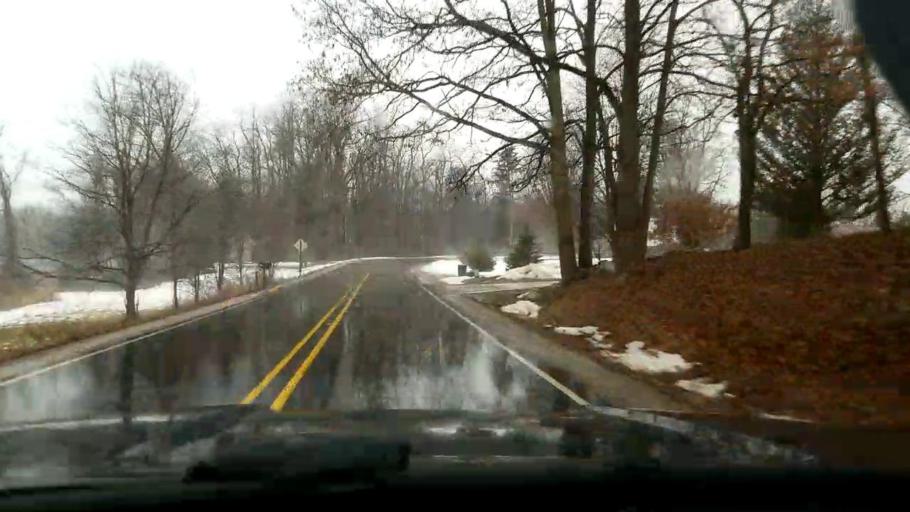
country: US
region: Michigan
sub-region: Jackson County
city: Michigan Center
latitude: 42.2849
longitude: -84.3297
